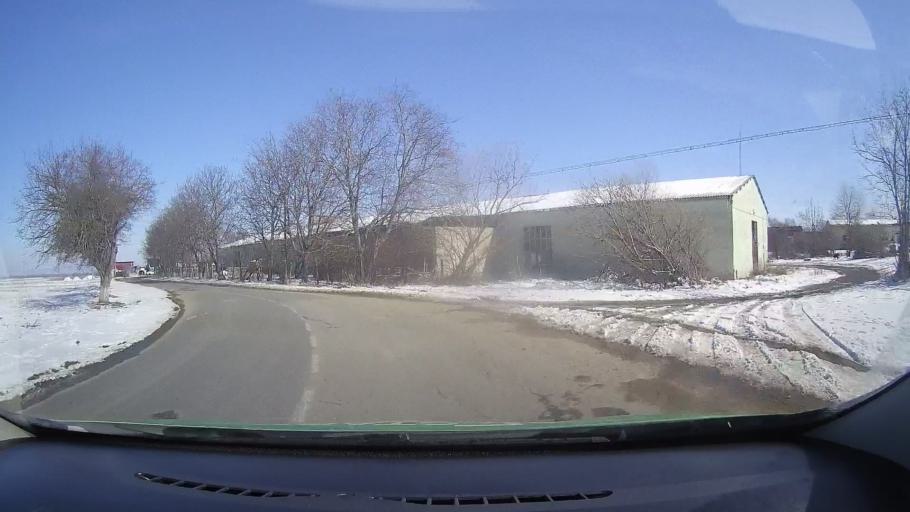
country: RO
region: Brasov
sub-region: Comuna Recea
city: Recea
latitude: 45.7329
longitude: 24.9328
